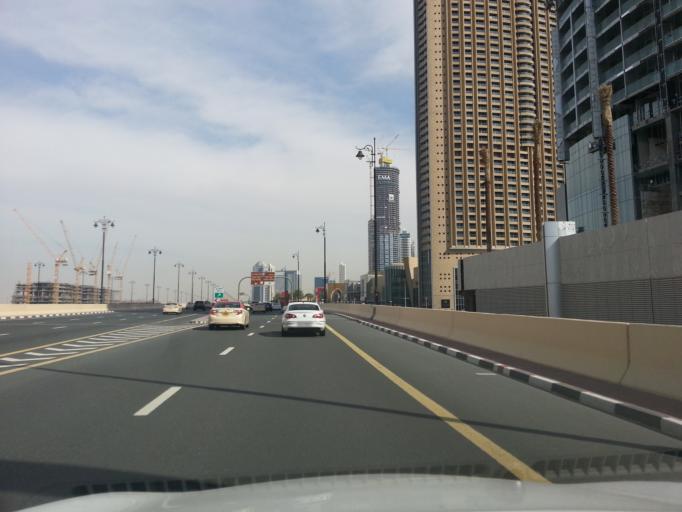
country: AE
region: Dubai
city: Dubai
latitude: 25.2017
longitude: 55.2761
